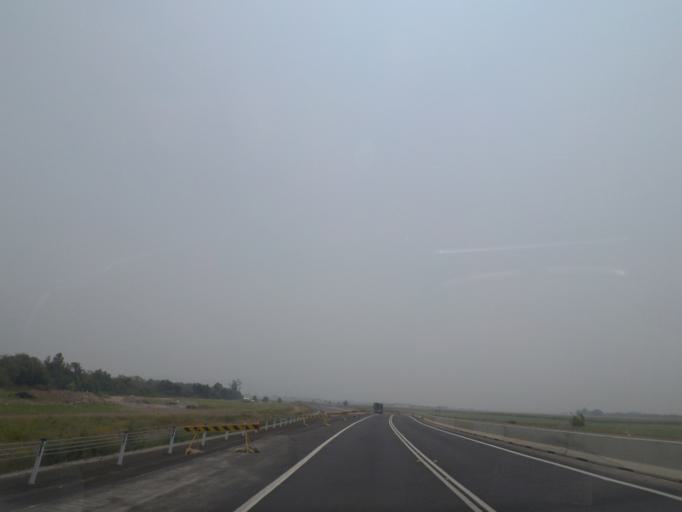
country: AU
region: New South Wales
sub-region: Clarence Valley
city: Maclean
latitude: -29.4037
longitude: 153.2423
